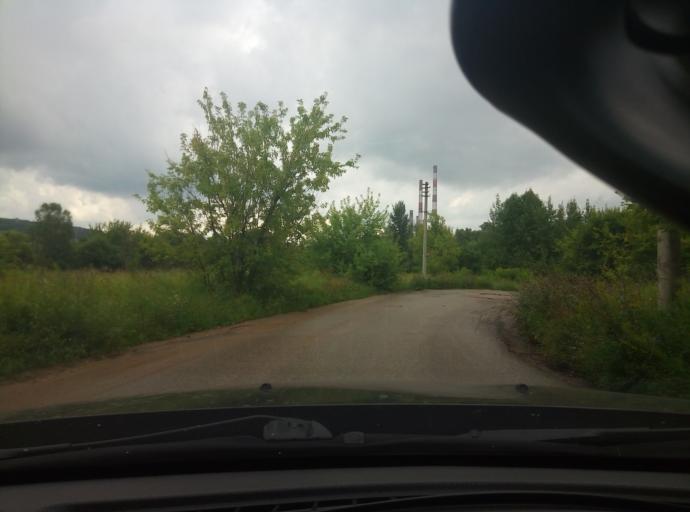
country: RU
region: Tula
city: Lomintsevskiy
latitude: 53.9589
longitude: 37.6440
